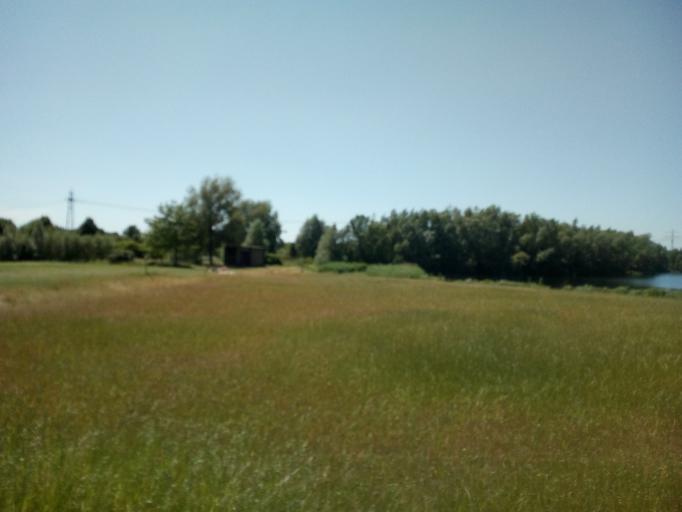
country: DE
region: Schleswig-Holstein
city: Oststeinbek
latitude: 53.4859
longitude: 10.1418
